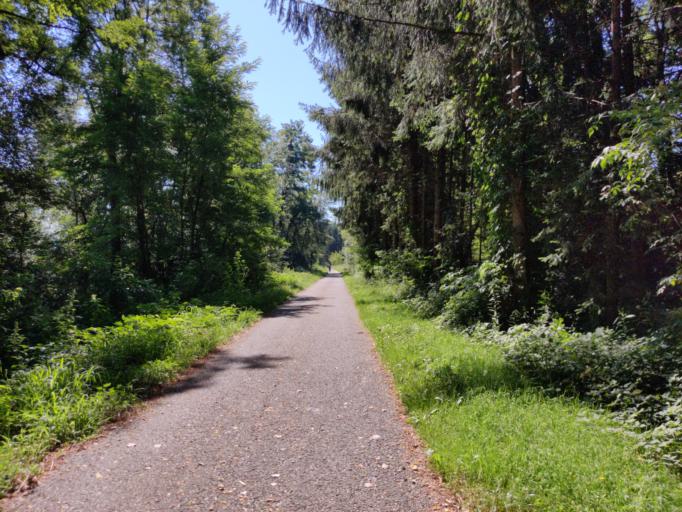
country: AT
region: Styria
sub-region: Politischer Bezirk Graz-Umgebung
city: Werndorf
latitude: 46.8994
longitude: 15.4952
